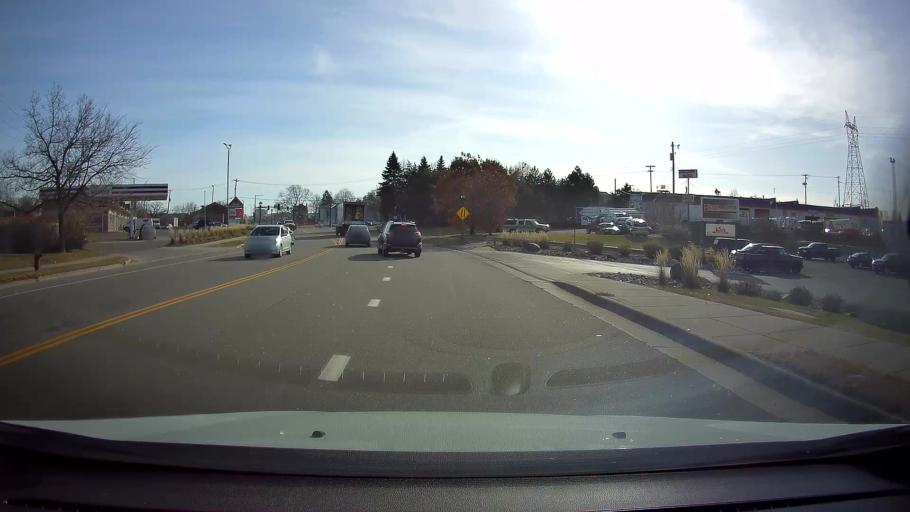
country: US
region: Minnesota
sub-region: Ramsey County
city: Lauderdale
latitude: 44.9747
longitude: -93.1966
